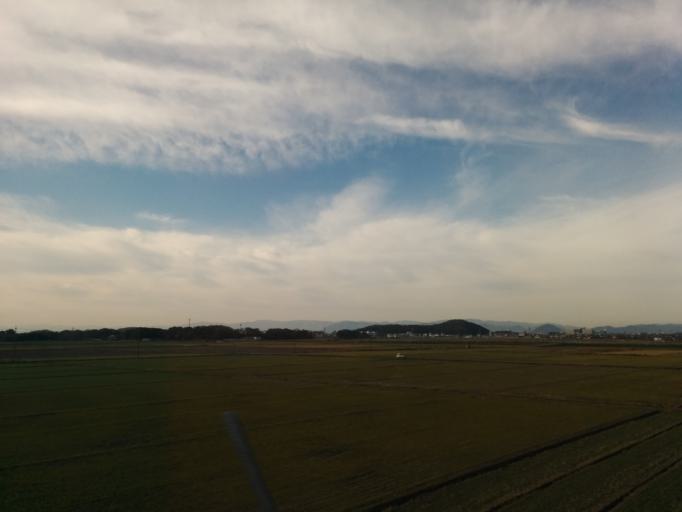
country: JP
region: Shiga Prefecture
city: Nagahama
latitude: 35.3479
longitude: 136.3062
